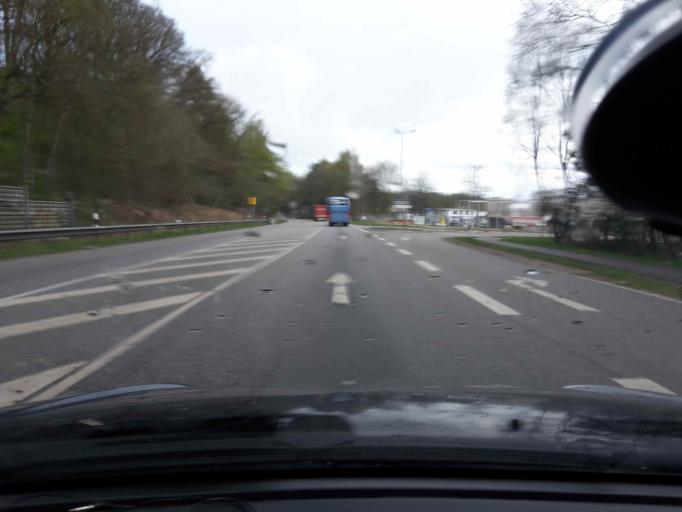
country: DE
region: Lower Saxony
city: Buxtehude
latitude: 53.4691
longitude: 9.6724
